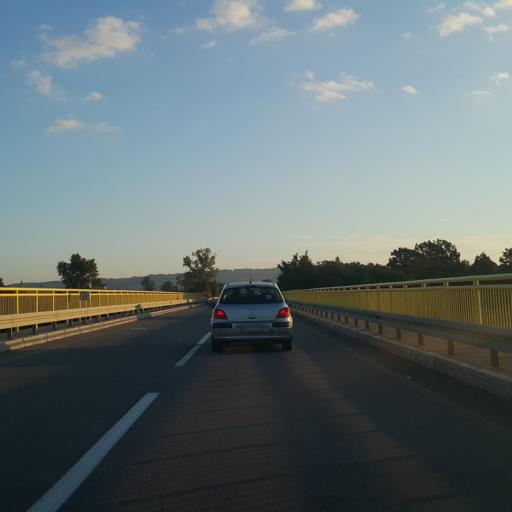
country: RS
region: Central Serbia
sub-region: Zajecarski Okrug
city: Zajecar
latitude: 44.0870
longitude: 22.3405
